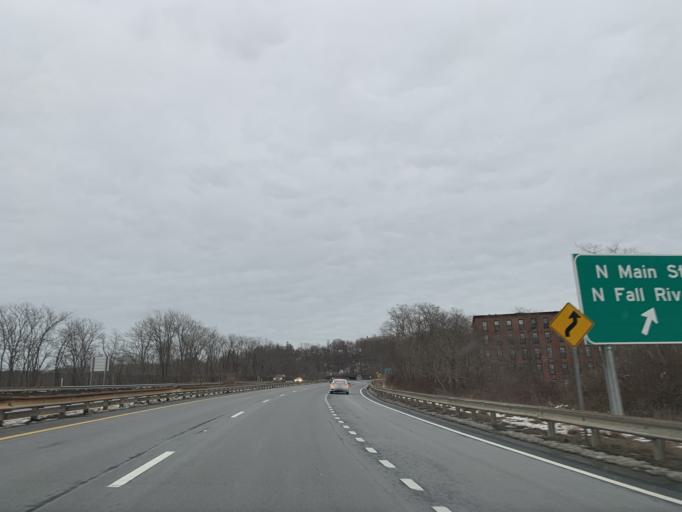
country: US
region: Massachusetts
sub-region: Bristol County
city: Fall River
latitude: 41.7292
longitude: -71.1431
